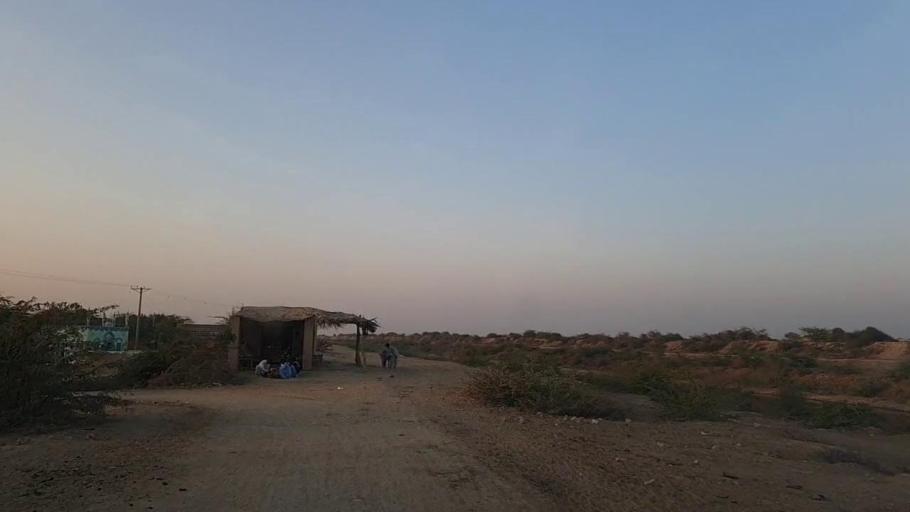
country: PK
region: Sindh
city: Naukot
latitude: 24.9529
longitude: 69.4279
